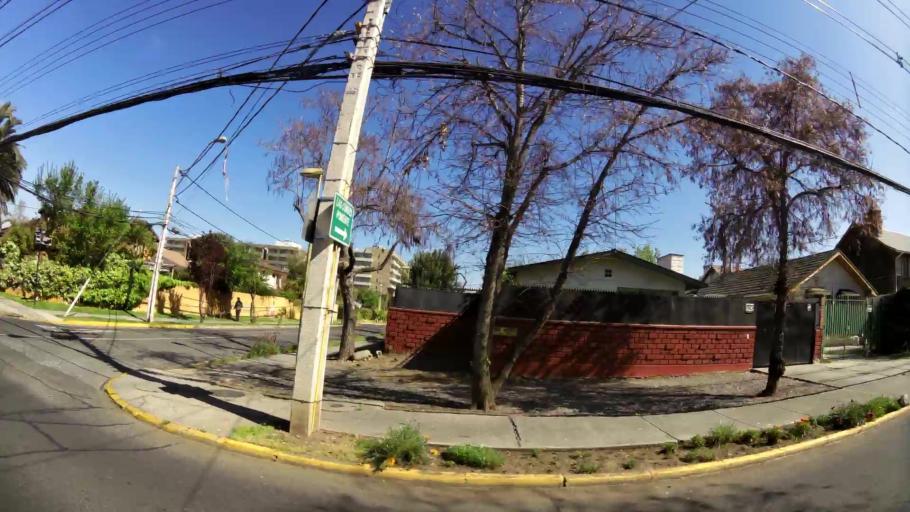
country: CL
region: Santiago Metropolitan
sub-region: Provincia de Santiago
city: Villa Presidente Frei, Nunoa, Santiago, Chile
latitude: -33.4021
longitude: -70.5524
